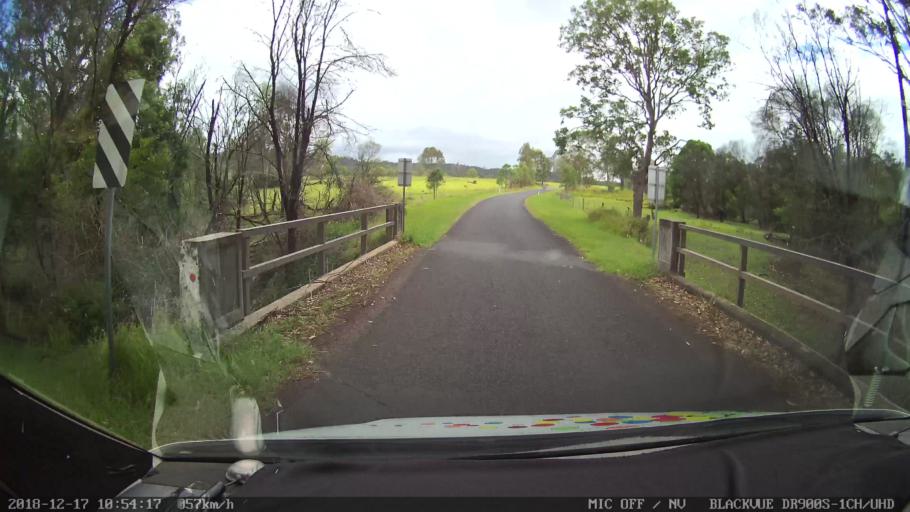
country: AU
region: New South Wales
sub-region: Tenterfield Municipality
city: Carrolls Creek
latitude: -28.8302
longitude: 152.5661
